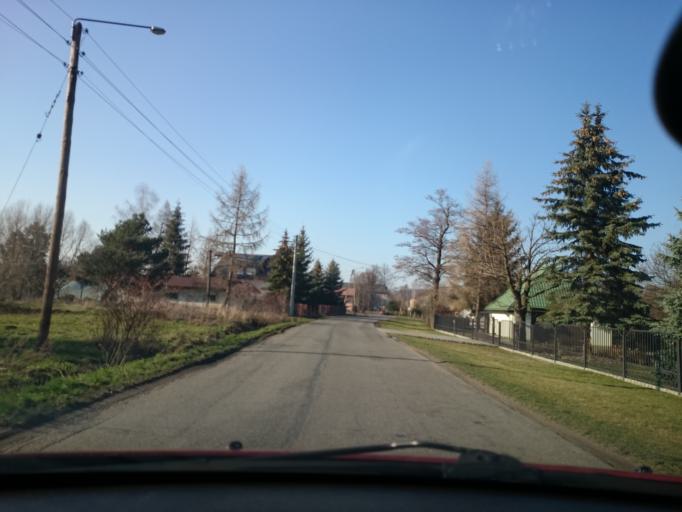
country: PL
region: Lower Silesian Voivodeship
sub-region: Powiat klodzki
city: Klodzko
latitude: 50.3777
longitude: 16.6367
